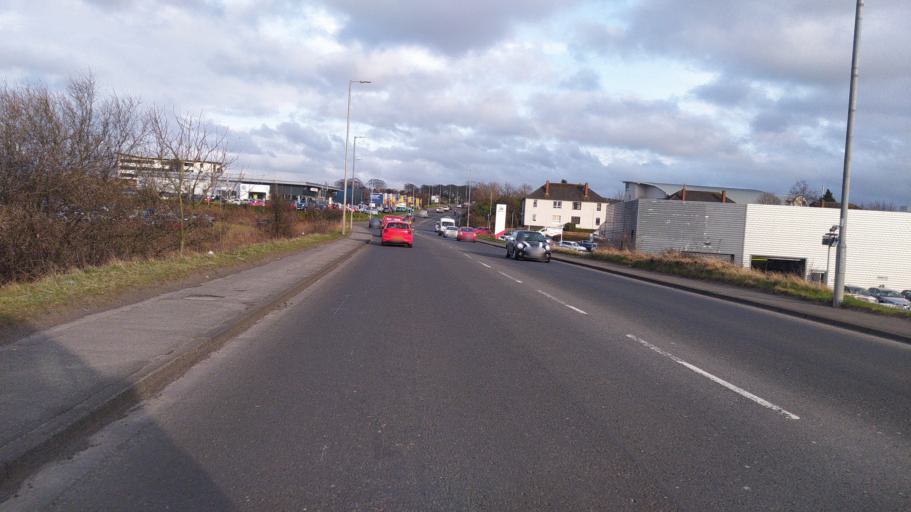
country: GB
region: Scotland
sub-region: South Ayrshire
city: Prestwick
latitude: 55.4772
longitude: -4.5922
